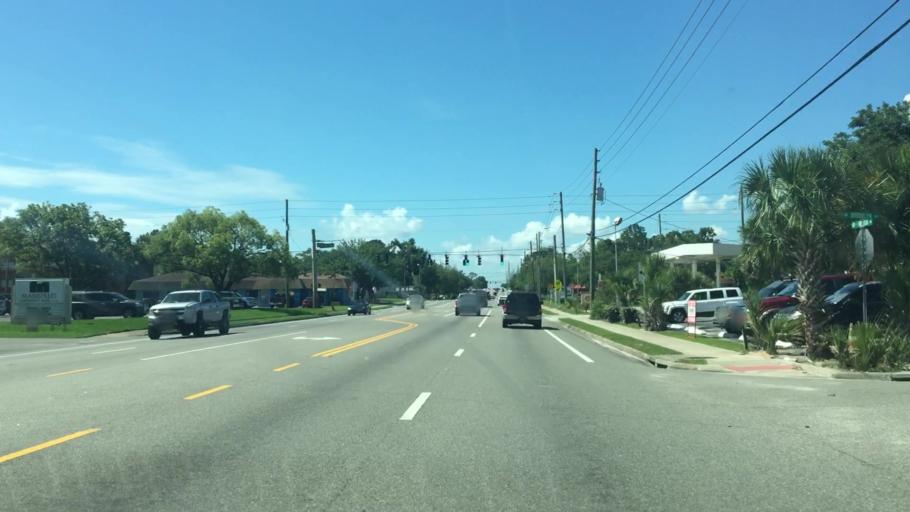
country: US
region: Florida
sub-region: Volusia County
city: Orange City
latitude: 28.9404
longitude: -81.2990
